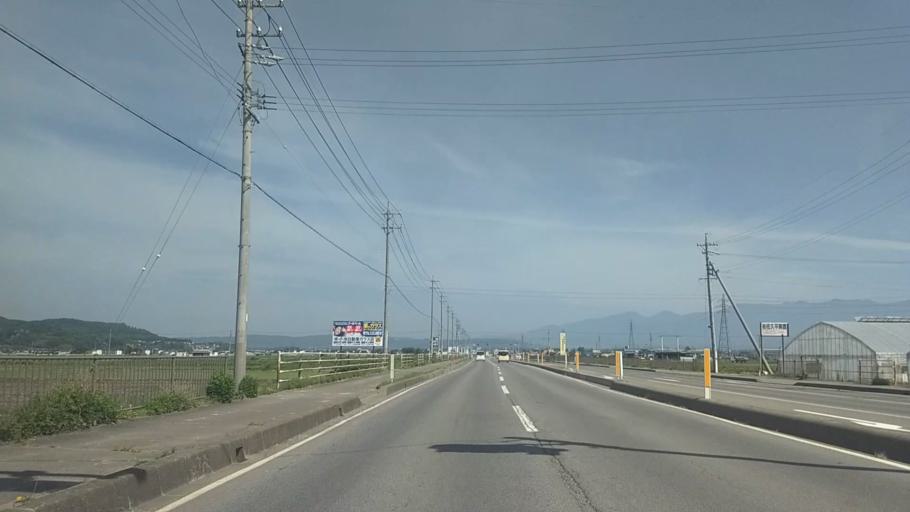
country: JP
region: Nagano
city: Saku
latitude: 36.2157
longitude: 138.4625
